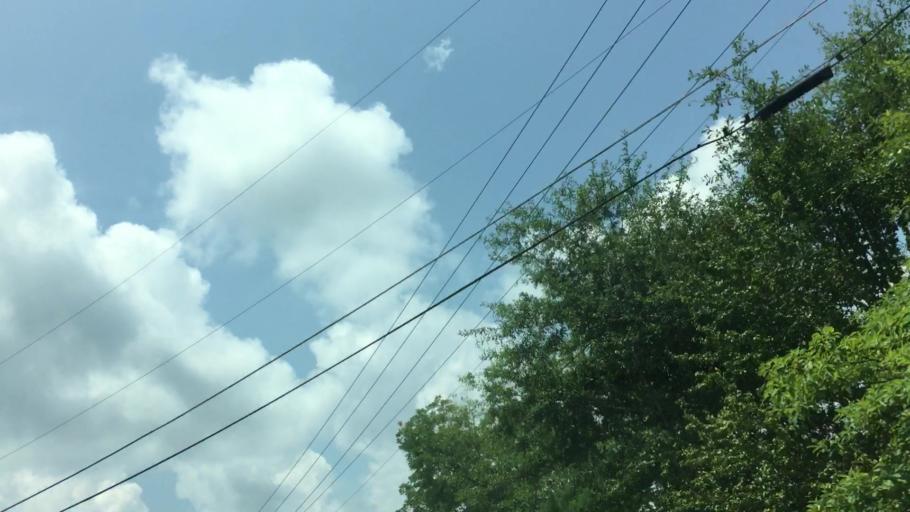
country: US
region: Georgia
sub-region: Fulton County
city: Chattahoochee Hills
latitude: 33.6168
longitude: -84.8445
